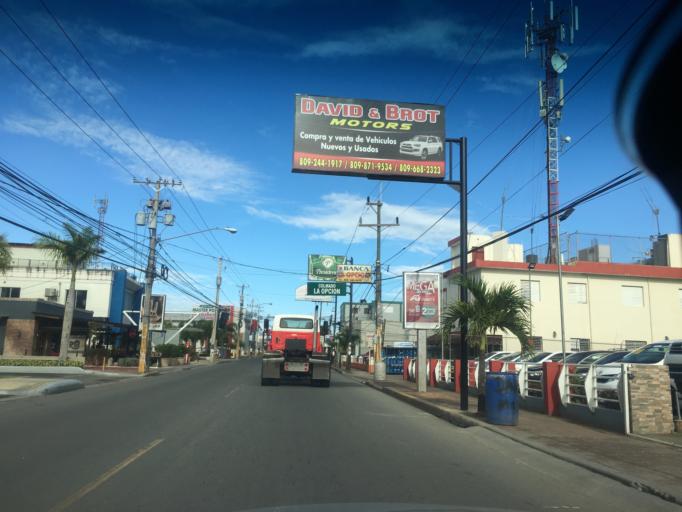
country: DO
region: Duarte
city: San Francisco de Macoris
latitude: 19.2855
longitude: -70.2757
